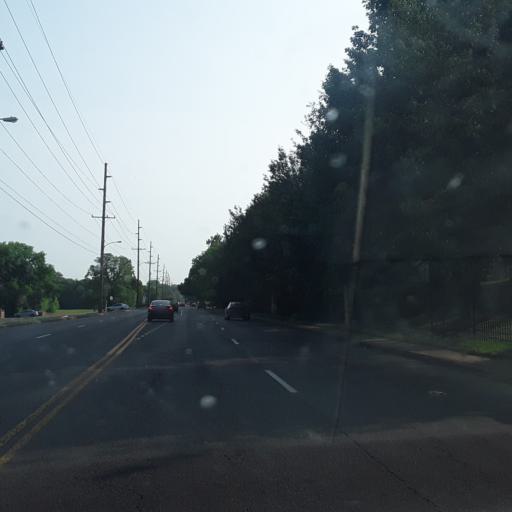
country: US
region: Tennessee
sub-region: Williamson County
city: Brentwood
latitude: 36.0594
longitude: -86.7415
